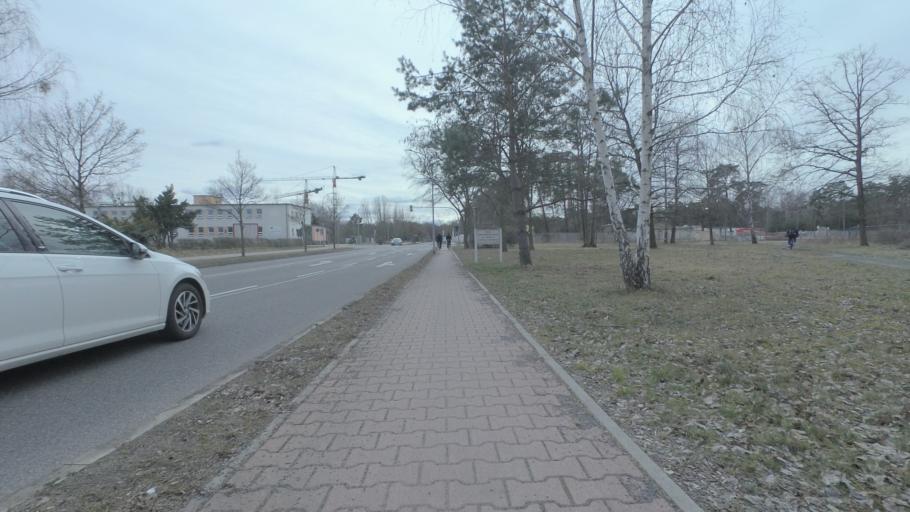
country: DE
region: Brandenburg
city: Ludwigsfelde
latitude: 52.3164
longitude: 13.2642
